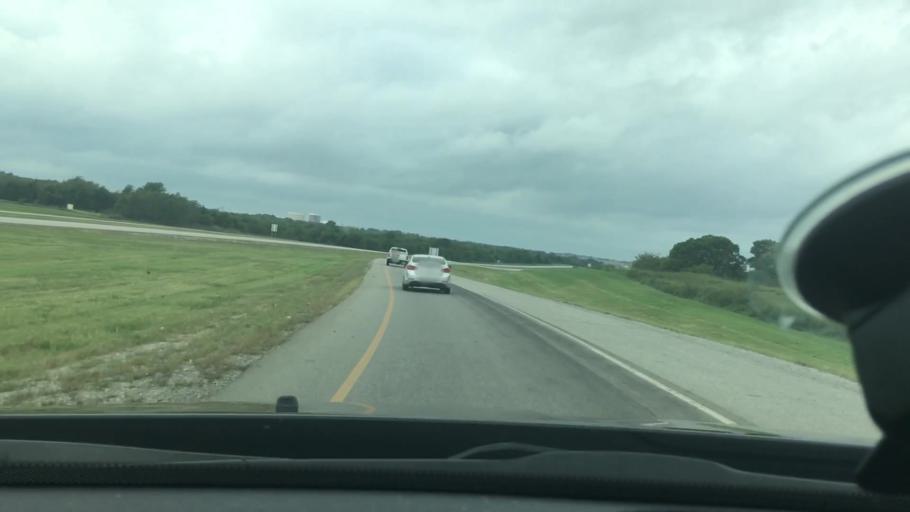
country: US
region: Oklahoma
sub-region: Bryan County
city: Durant
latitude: 33.9663
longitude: -96.3741
